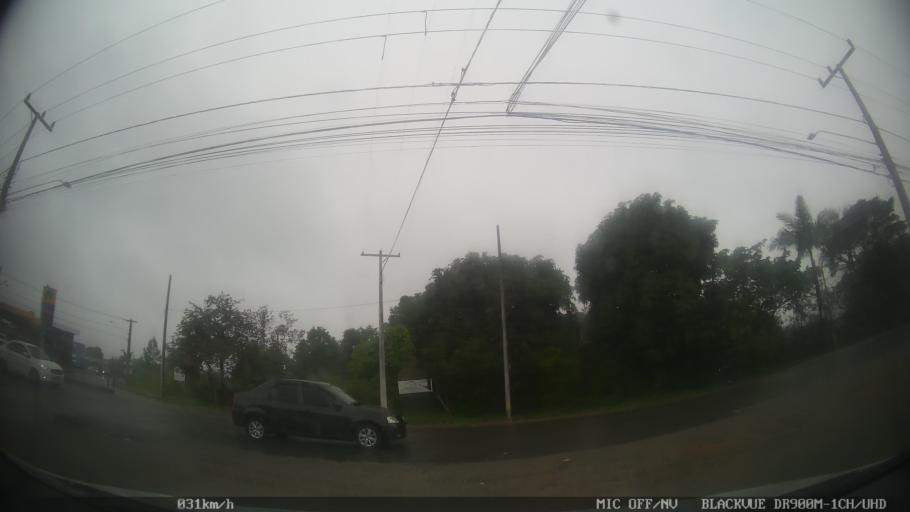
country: BR
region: Santa Catarina
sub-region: Joinville
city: Joinville
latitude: -26.2183
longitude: -48.8188
